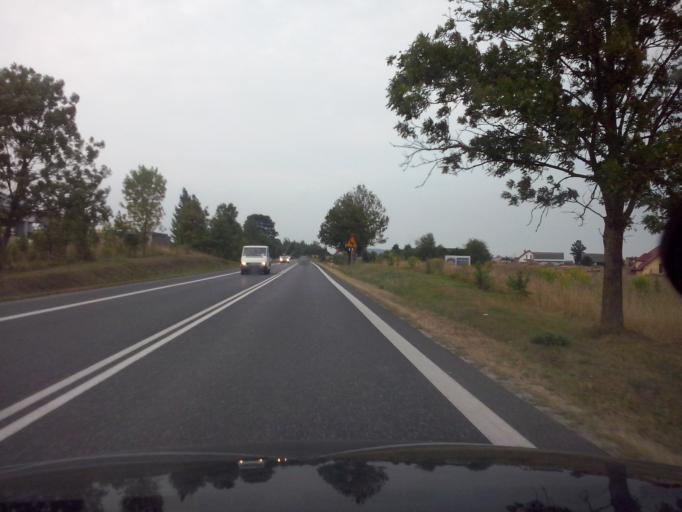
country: PL
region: Swietokrzyskie
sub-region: Powiat kielecki
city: Morawica
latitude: 50.7759
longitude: 20.6195
